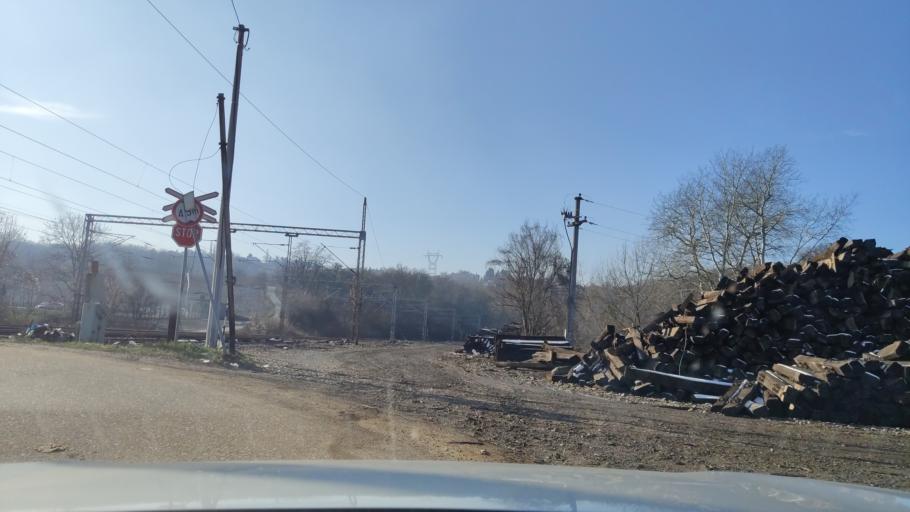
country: RS
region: Central Serbia
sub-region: Belgrade
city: Zvezdara
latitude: 44.7144
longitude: 20.5159
